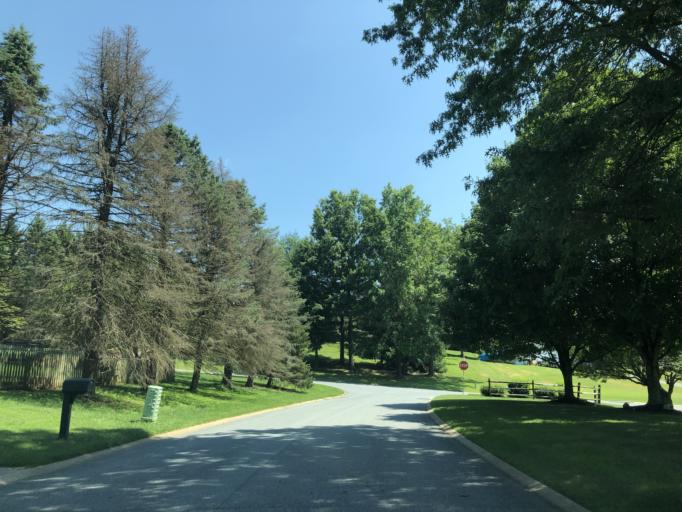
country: US
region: Maryland
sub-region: Carroll County
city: Eldersburg
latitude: 39.4302
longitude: -76.9715
